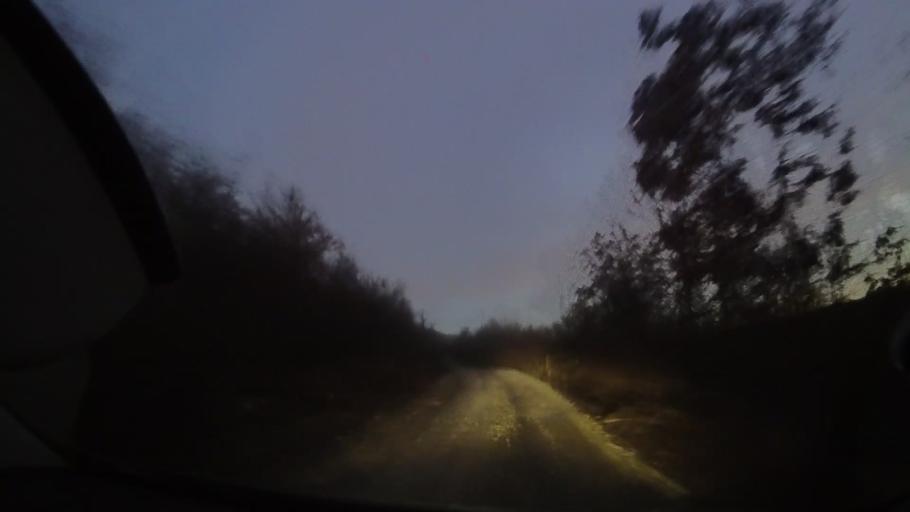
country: RO
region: Bihor
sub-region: Comuna Tetchea
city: Hotar
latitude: 47.0008
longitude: 22.3102
